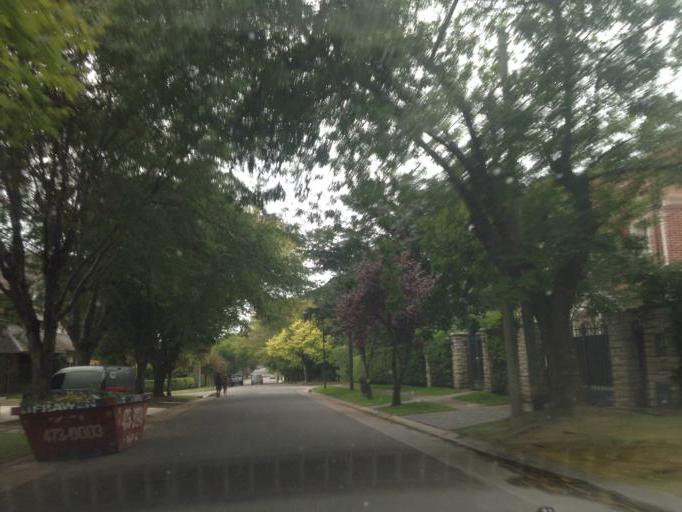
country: AR
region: Buenos Aires
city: Mar del Plata
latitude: -38.0253
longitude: -57.5395
